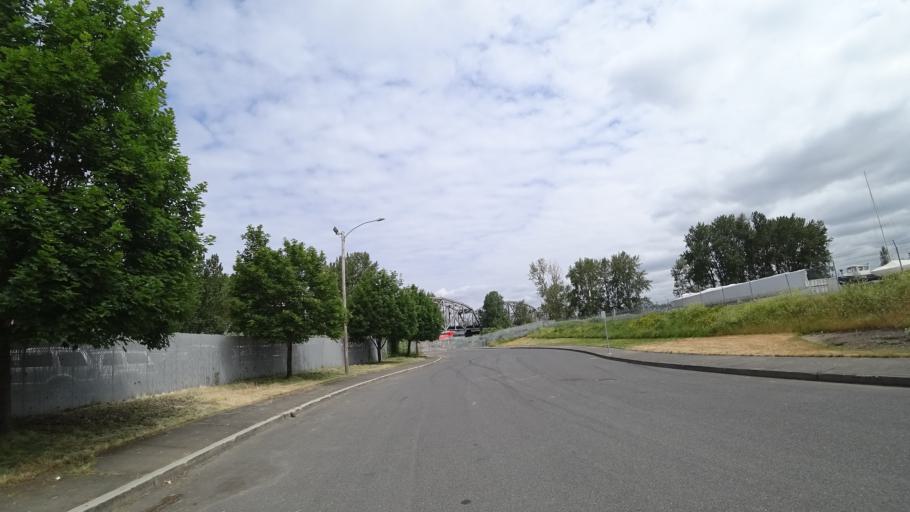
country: US
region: Washington
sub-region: Clark County
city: Vancouver
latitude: 45.6205
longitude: -122.6939
